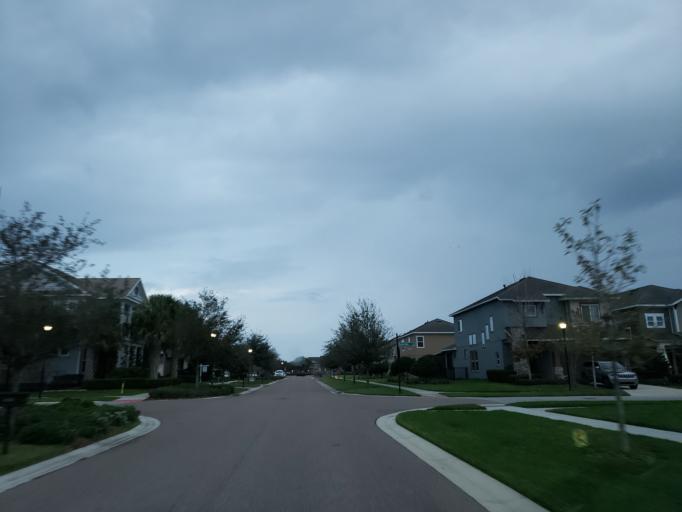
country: US
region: Florida
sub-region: Hillsborough County
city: Fish Hawk
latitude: 27.8480
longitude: -82.2534
